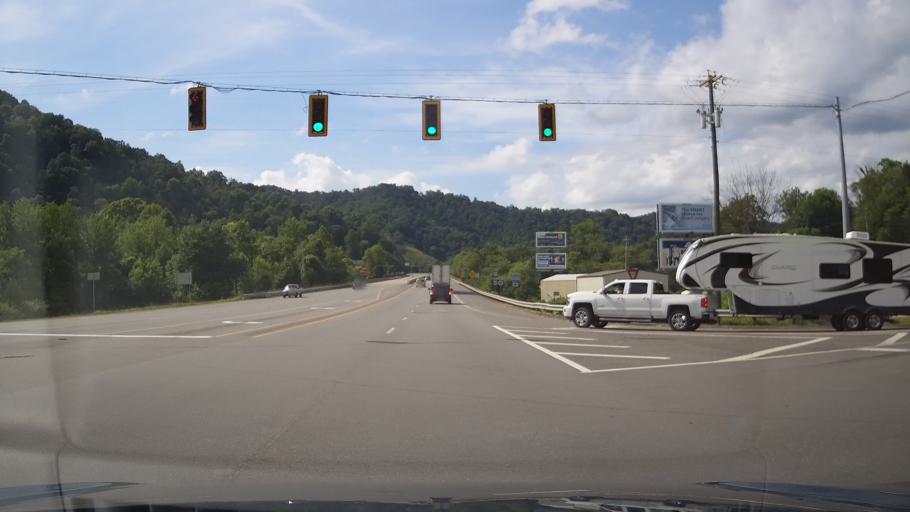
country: US
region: Kentucky
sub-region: Floyd County
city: Prestonsburg
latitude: 37.6168
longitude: -82.7216
